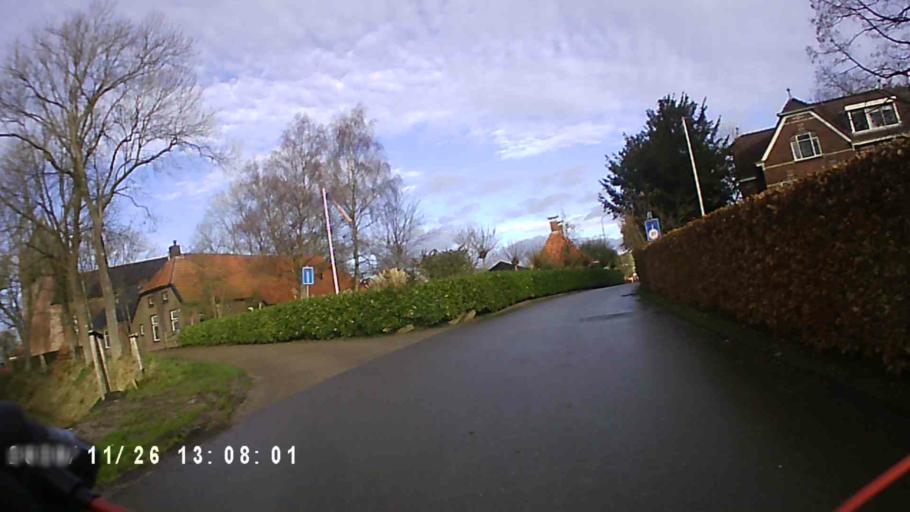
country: NL
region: Groningen
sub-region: Gemeente Appingedam
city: Appingedam
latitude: 53.3544
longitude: 6.8490
